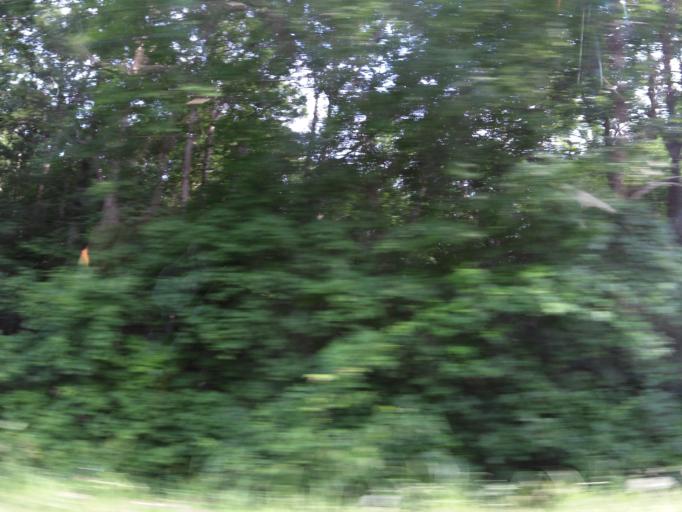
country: US
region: Tennessee
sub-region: Humphreys County
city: McEwen
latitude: 36.1035
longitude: -87.6795
